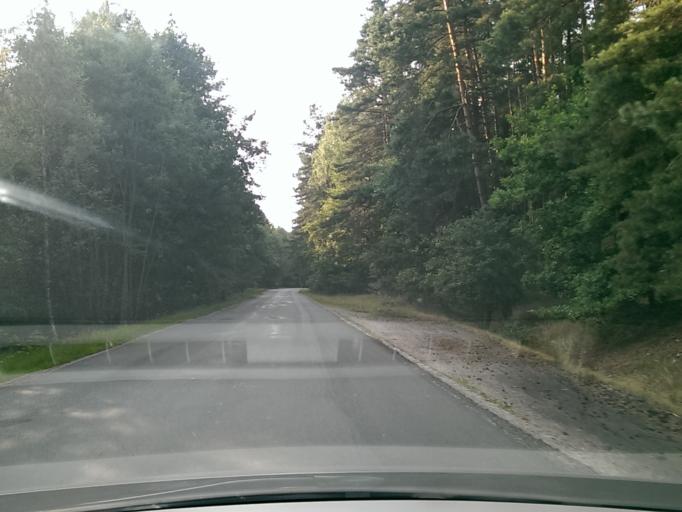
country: CZ
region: Central Bohemia
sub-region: Okres Mlada Boleslav
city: Zd'ar
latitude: 50.5171
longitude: 15.1124
